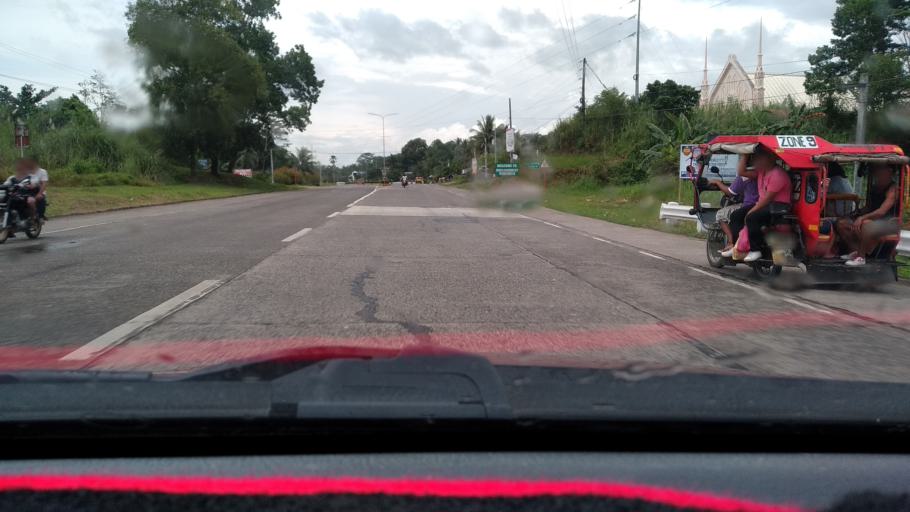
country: PH
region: Caraga
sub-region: Province of Agusan del Sur
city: San Francisco
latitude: 8.5392
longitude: 125.9474
